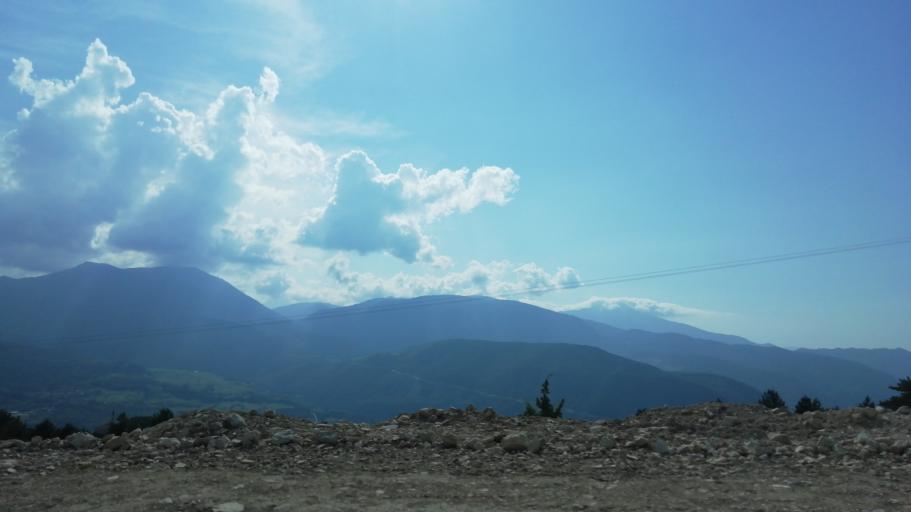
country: TR
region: Karabuk
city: Karabuk
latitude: 41.1184
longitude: 32.5810
